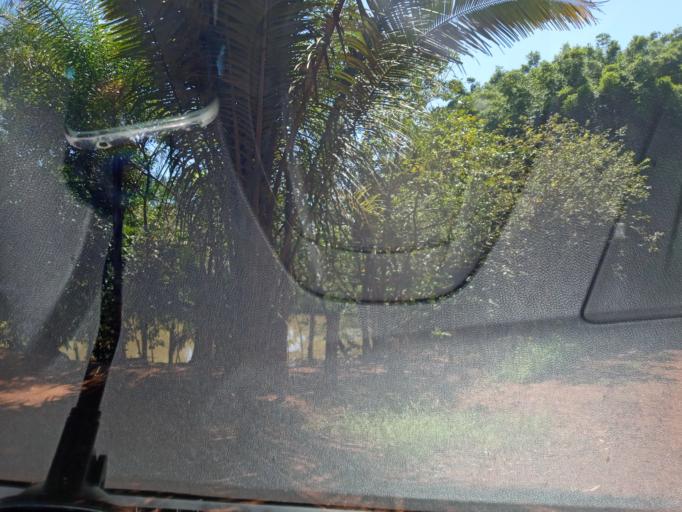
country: BR
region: Goias
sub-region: Itumbiara
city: Itumbiara
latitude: -18.4405
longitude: -49.1437
